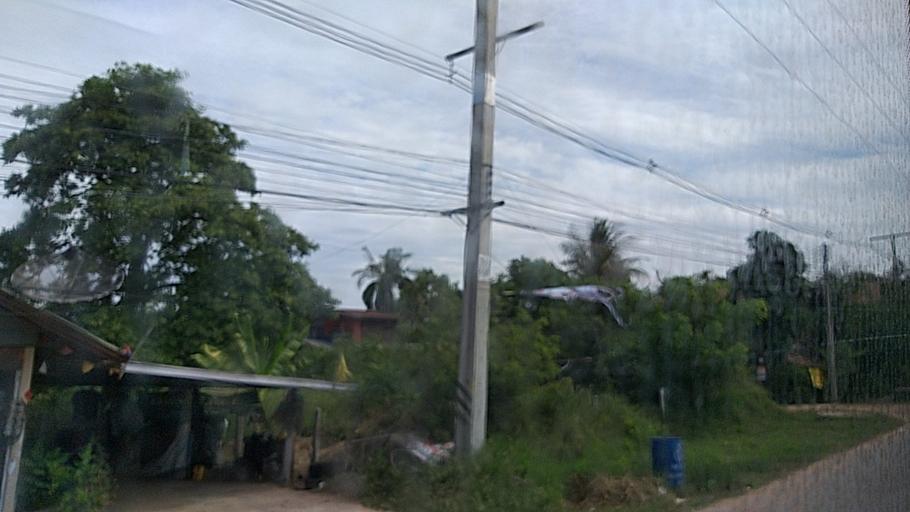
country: TH
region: Maha Sarakham
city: Chiang Yuen
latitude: 16.4206
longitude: 103.0757
